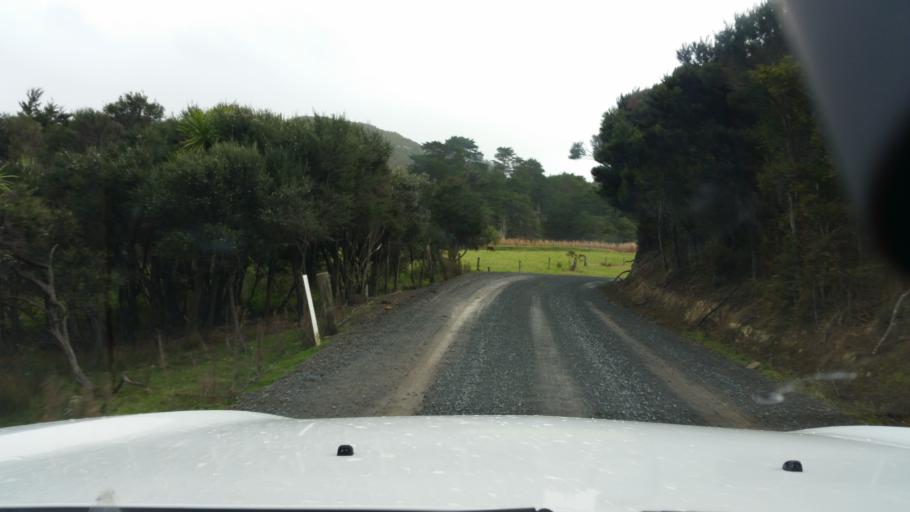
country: NZ
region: Northland
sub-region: Whangarei
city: Ruakaka
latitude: -35.7795
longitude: 174.5450
